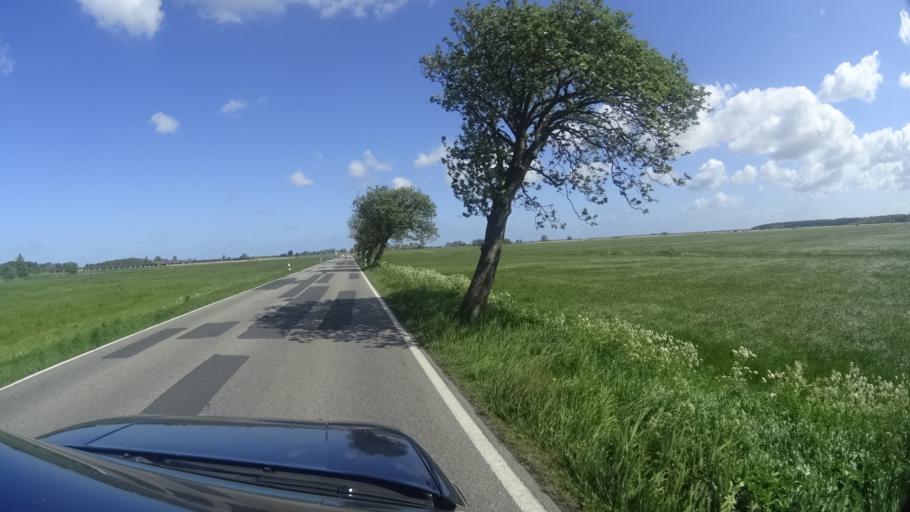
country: DE
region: Mecklenburg-Vorpommern
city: Zingst
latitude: 54.3865
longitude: 12.6776
